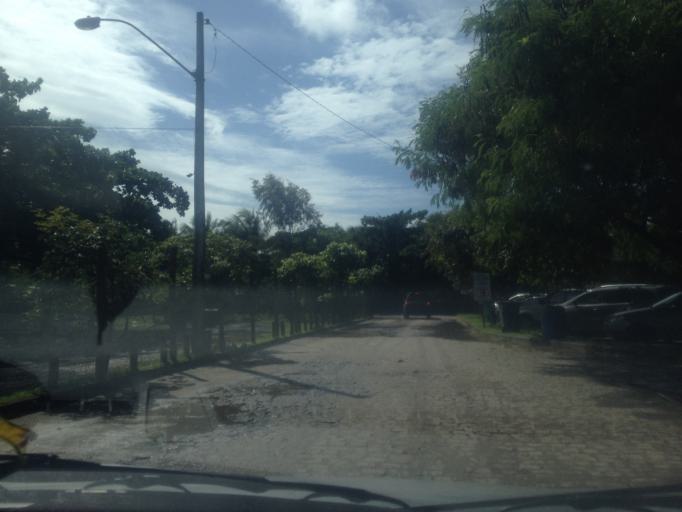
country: BR
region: Bahia
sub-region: Mata De Sao Joao
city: Mata de Sao Joao
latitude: -12.5763
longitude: -38.0043
